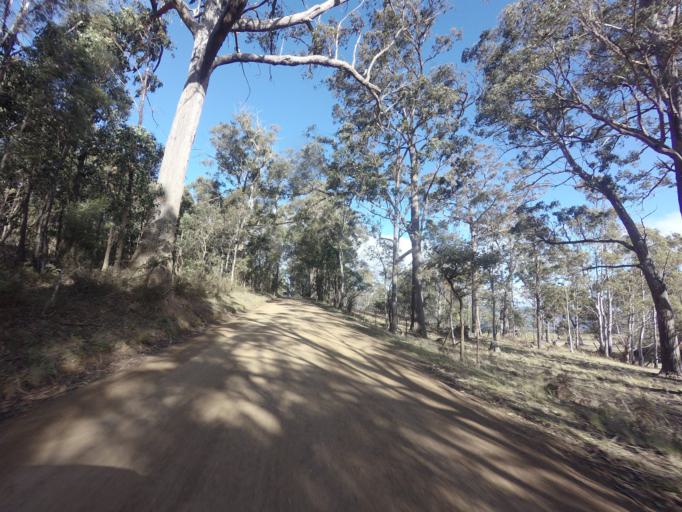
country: AU
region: Tasmania
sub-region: Derwent Valley
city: New Norfolk
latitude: -42.7141
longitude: 147.0314
